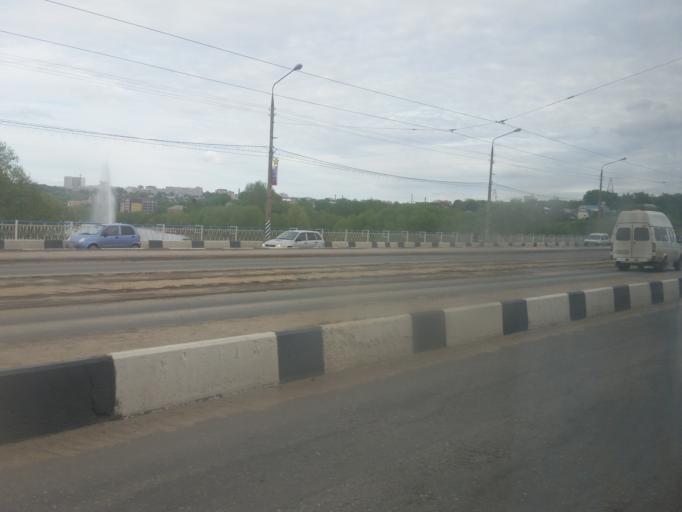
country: RU
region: Ulyanovsk
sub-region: Ulyanovskiy Rayon
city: Ulyanovsk
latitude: 54.3056
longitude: 48.3640
